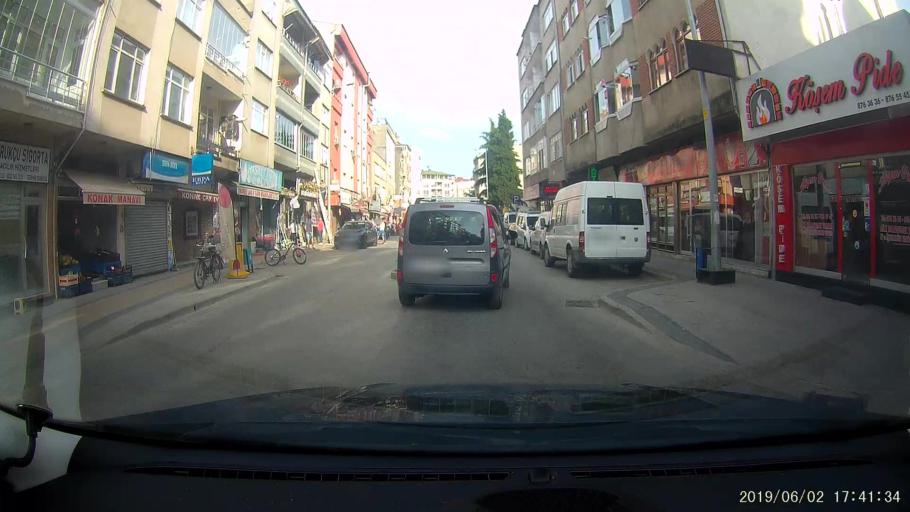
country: TR
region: Samsun
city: Terme
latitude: 41.2101
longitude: 36.9701
